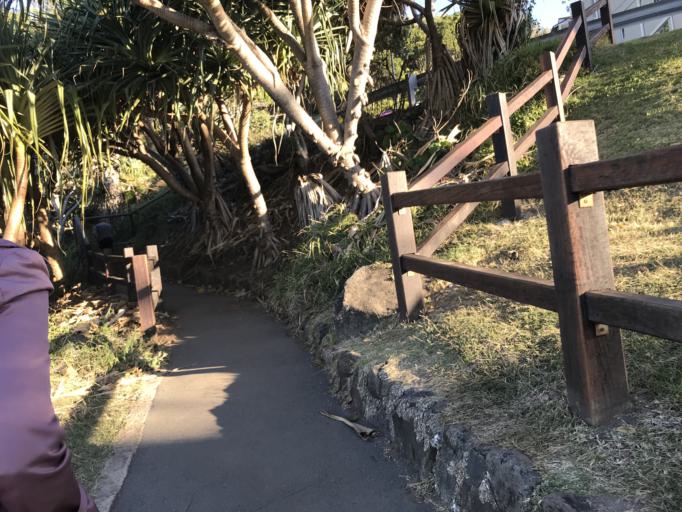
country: AU
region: Queensland
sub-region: Gold Coast
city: Palm Beach
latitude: -28.0902
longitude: 153.4579
